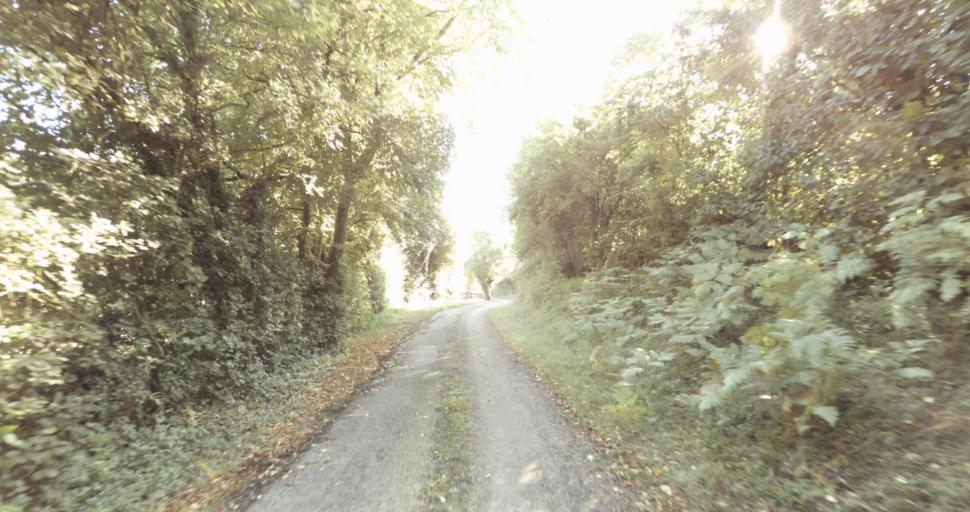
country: FR
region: Lower Normandy
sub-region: Departement de l'Orne
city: Vimoutiers
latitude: 48.8974
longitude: 0.1447
